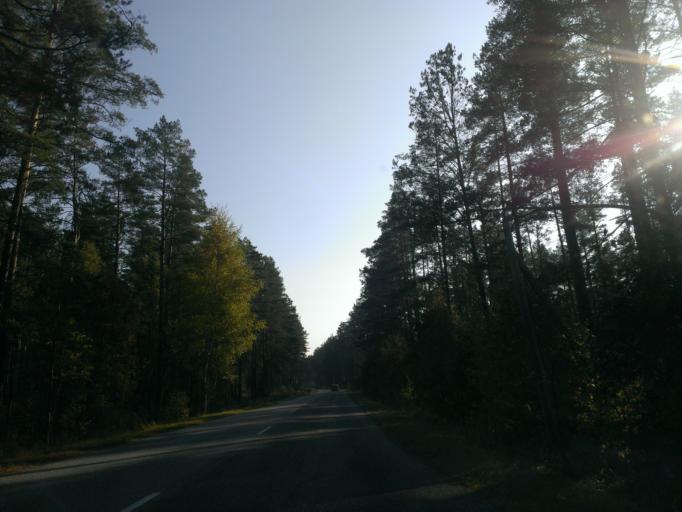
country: LV
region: Garkalne
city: Garkalne
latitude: 57.0254
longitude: 24.4315
